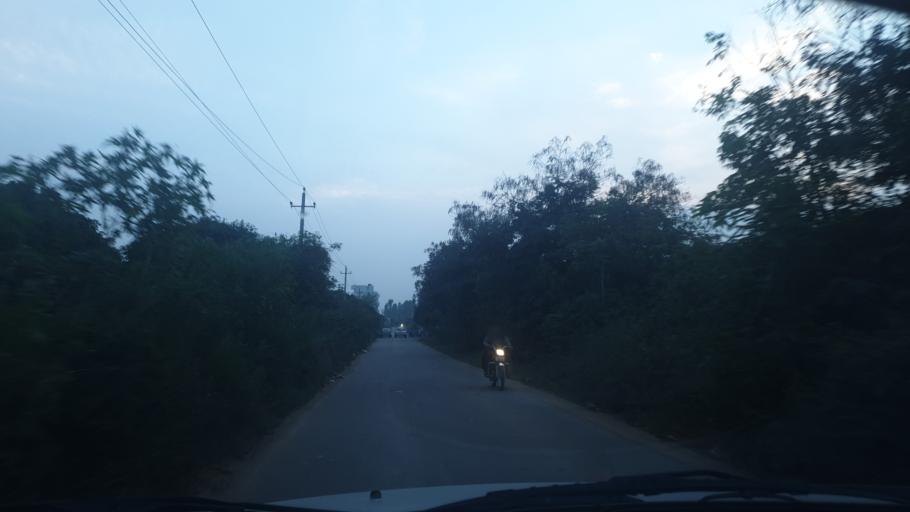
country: IN
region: Karnataka
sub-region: Bangalore Urban
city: Yelahanka
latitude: 13.0639
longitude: 77.6878
